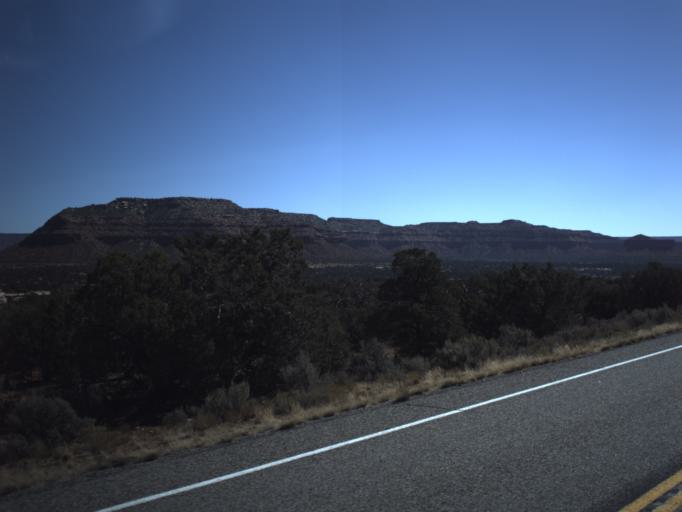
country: US
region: Utah
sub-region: San Juan County
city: Blanding
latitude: 37.6533
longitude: -110.1726
